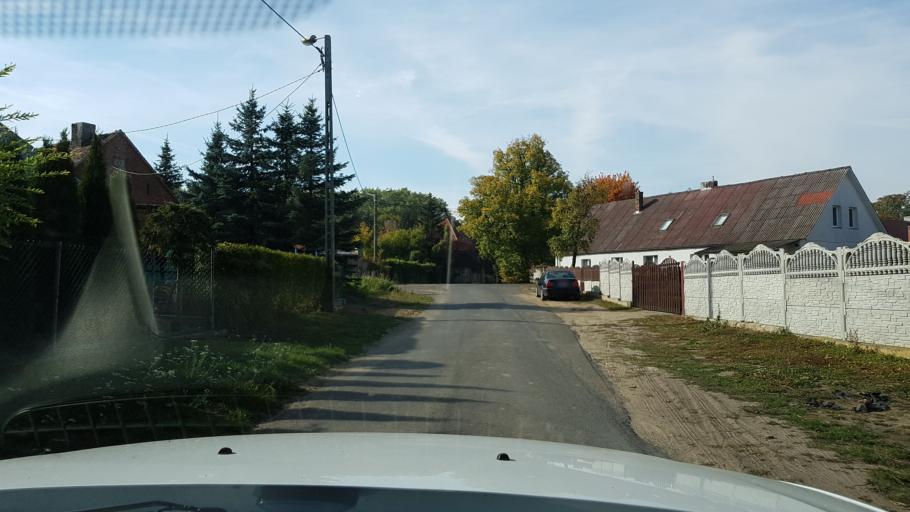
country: PL
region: West Pomeranian Voivodeship
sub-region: Powiat pyrzycki
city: Lipiany
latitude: 52.9310
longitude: 14.9443
